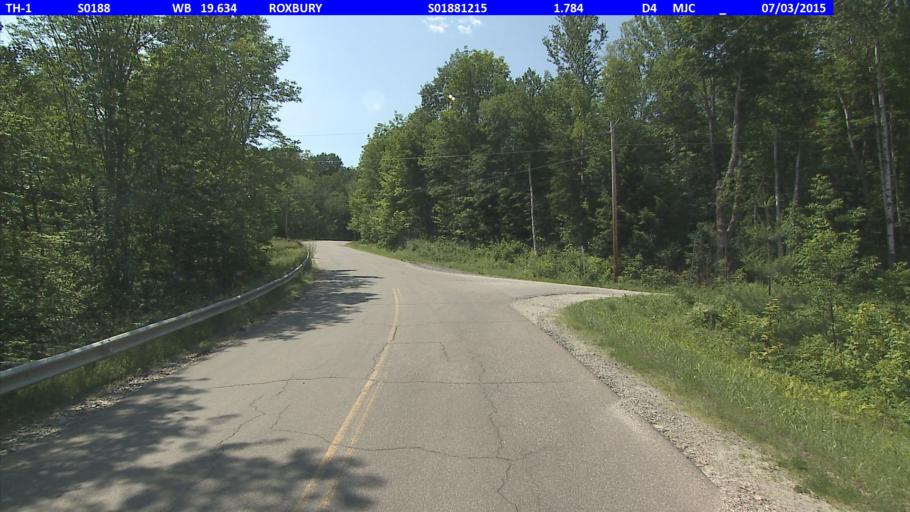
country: US
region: Vermont
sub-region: Washington County
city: Northfield
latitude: 44.1054
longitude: -72.7498
